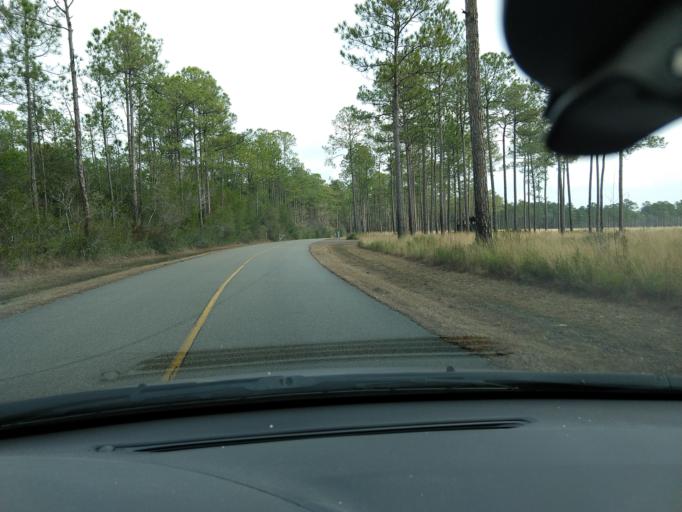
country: US
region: Mississippi
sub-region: Jackson County
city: Hickory Hills
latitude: 30.4466
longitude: -88.6611
